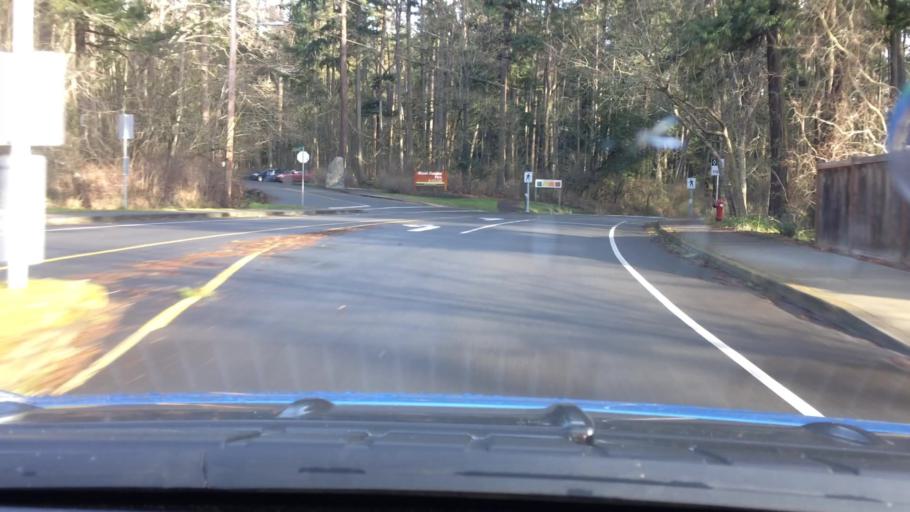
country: CA
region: British Columbia
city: Oak Bay
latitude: 48.4903
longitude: -123.3380
